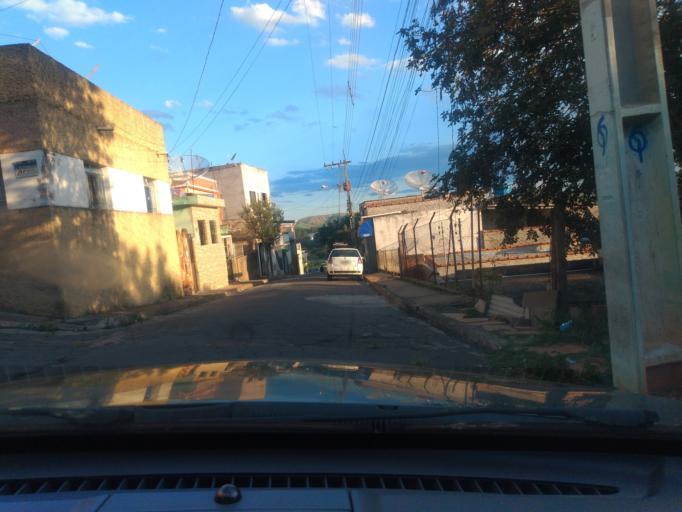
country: BR
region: Minas Gerais
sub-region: Tres Coracoes
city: Tres Coracoes
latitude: -21.6964
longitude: -45.2493
